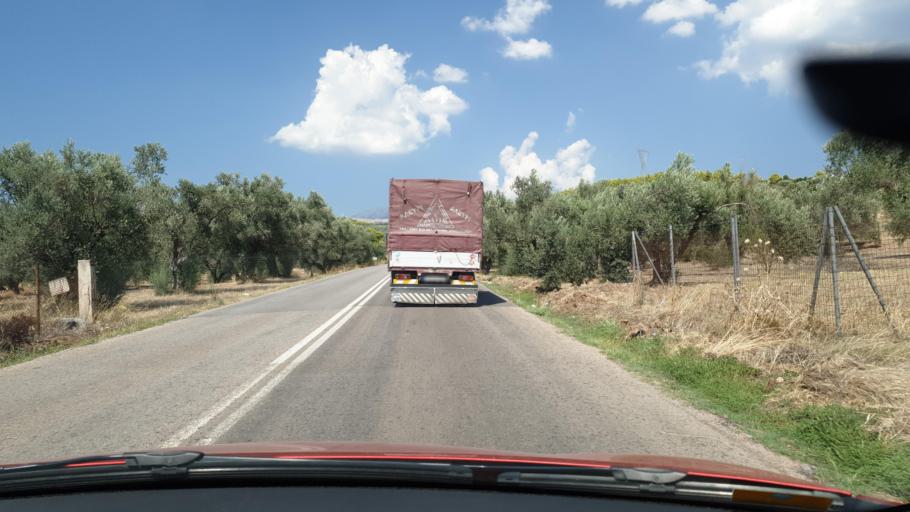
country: GR
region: Central Greece
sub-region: Nomos Evvoias
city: Psachna
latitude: 38.5828
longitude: 23.6103
